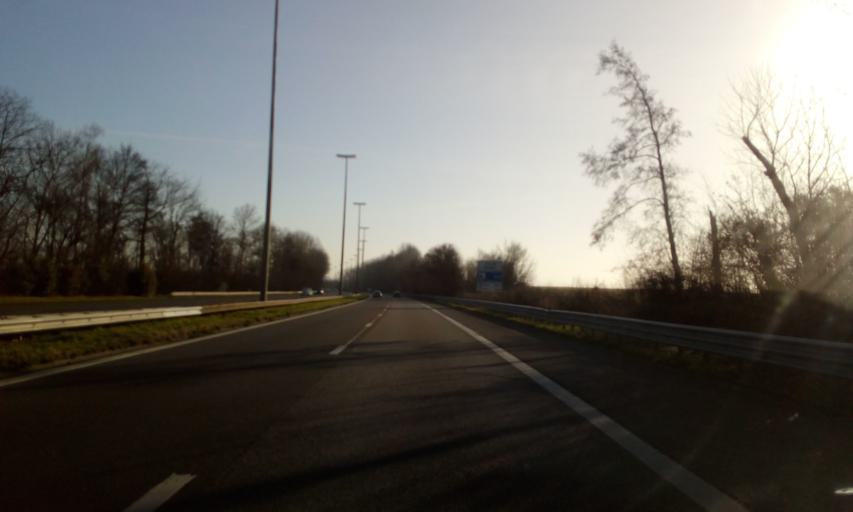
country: BE
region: Wallonia
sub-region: Province du Hainaut
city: Pont-a-Celles
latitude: 50.5293
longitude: 4.3827
